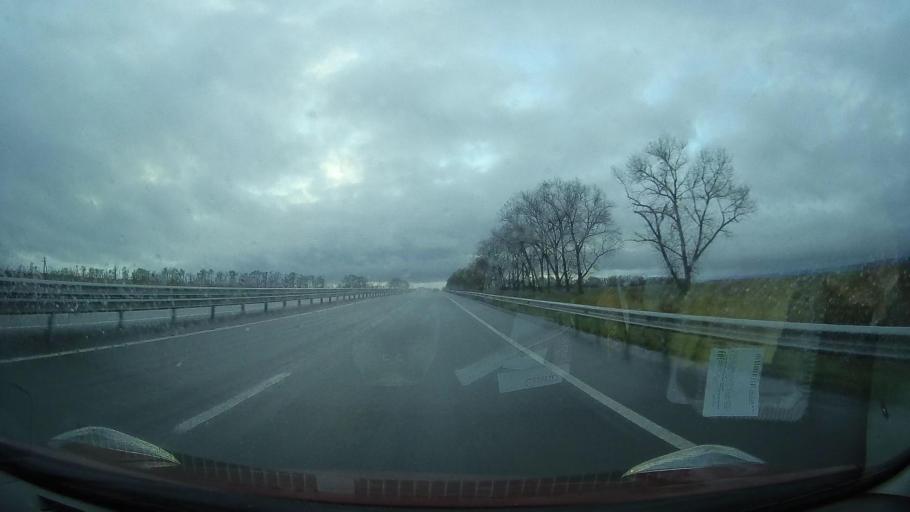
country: RU
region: Stavropol'skiy
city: Zavetnoye
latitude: 44.7865
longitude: 41.5139
